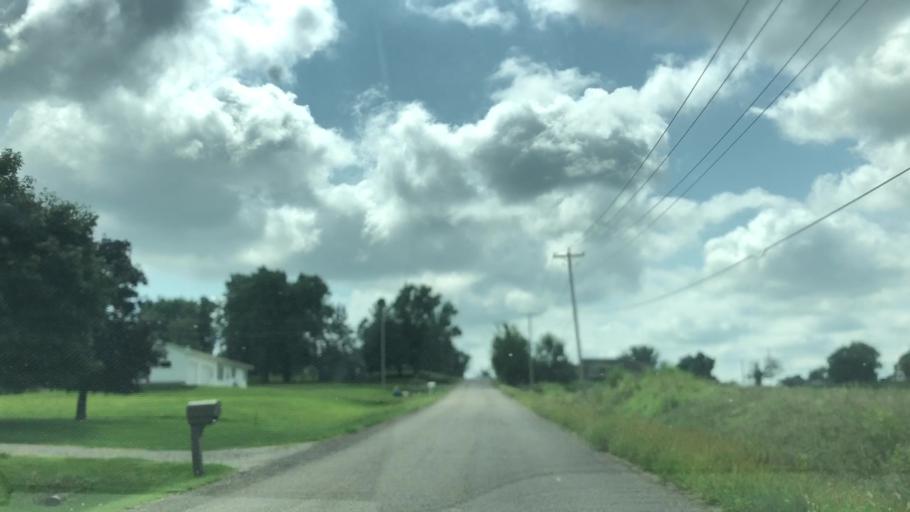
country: US
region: Iowa
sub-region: Marshall County
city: Marshalltown
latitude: 42.0519
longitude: -92.9565
